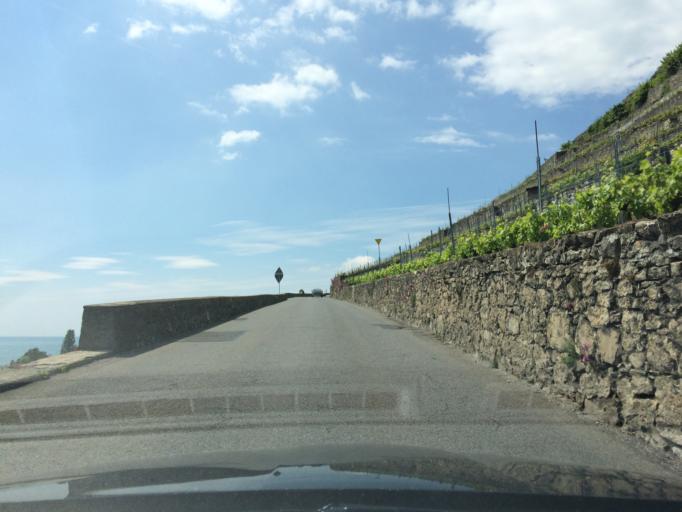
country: CH
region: Vaud
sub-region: Riviera-Pays-d'Enhaut District
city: Chardonne
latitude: 46.4713
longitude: 6.8123
